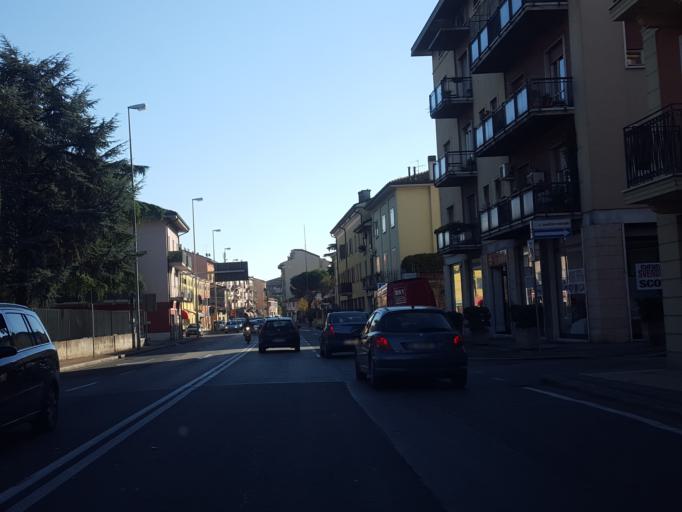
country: IT
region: Veneto
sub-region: Provincia di Verona
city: Verona
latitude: 45.4191
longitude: 10.9886
